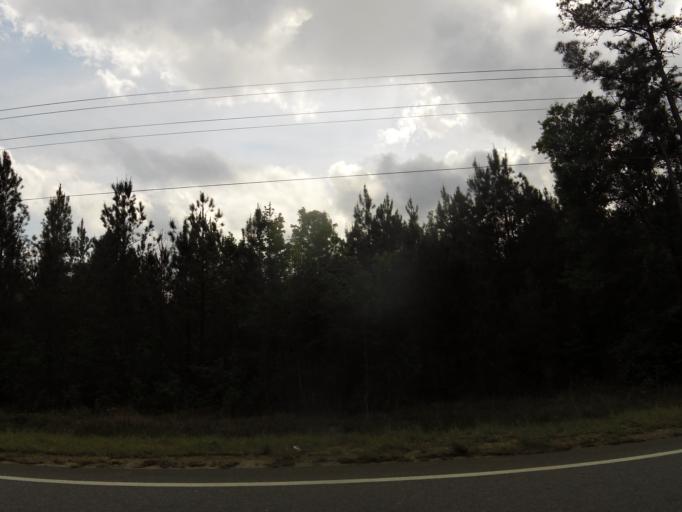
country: US
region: Florida
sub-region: Nassau County
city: Hilliard
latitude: 30.8202
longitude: -81.8547
